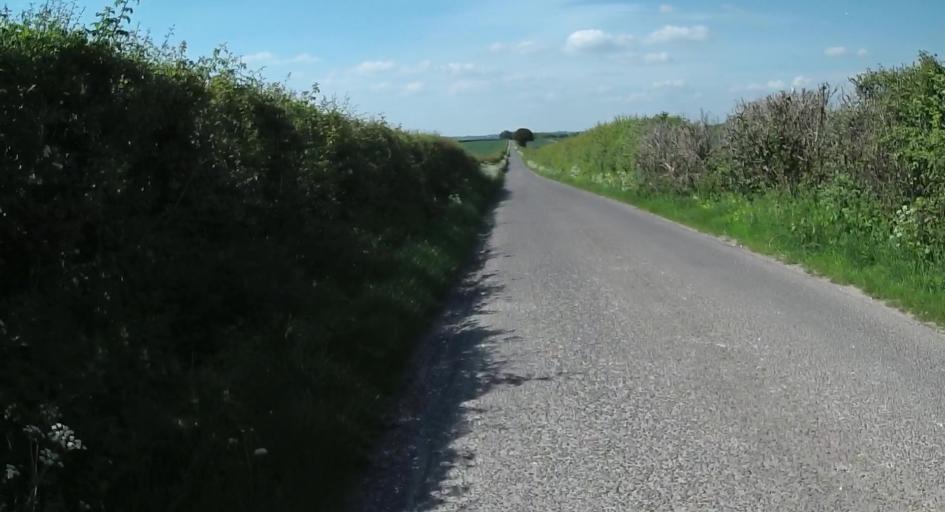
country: GB
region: England
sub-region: Hampshire
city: Kings Worthy
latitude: 51.0722
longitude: -1.2767
